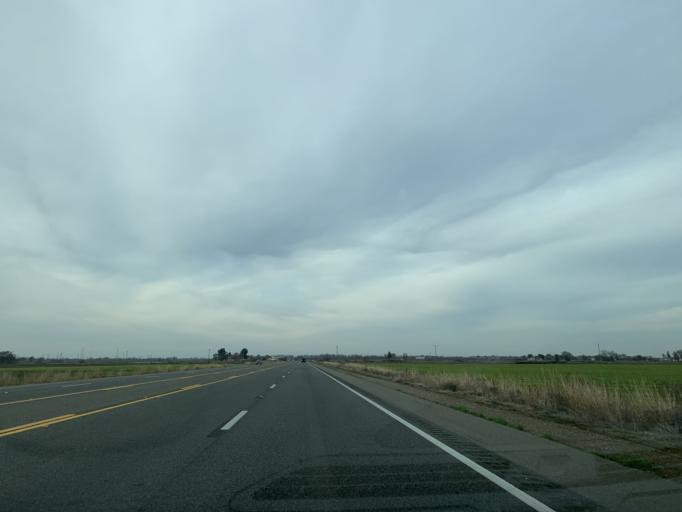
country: US
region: California
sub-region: Yuba County
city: Plumas Lake
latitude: 38.8781
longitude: -121.5642
